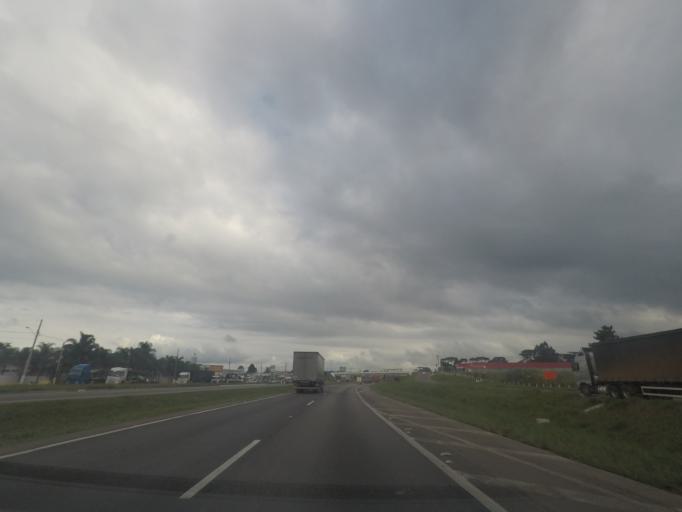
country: BR
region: Parana
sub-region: Sao Jose Dos Pinhais
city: Sao Jose dos Pinhais
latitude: -25.5573
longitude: -49.1501
